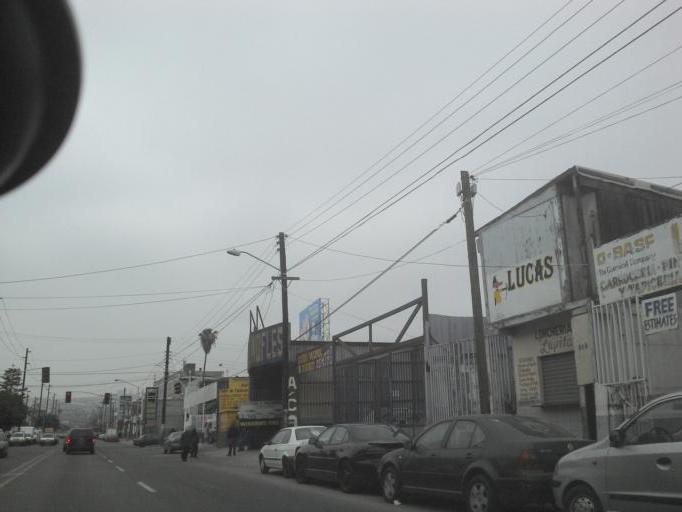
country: MX
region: Baja California
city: Tijuana
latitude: 32.5352
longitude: -117.0321
